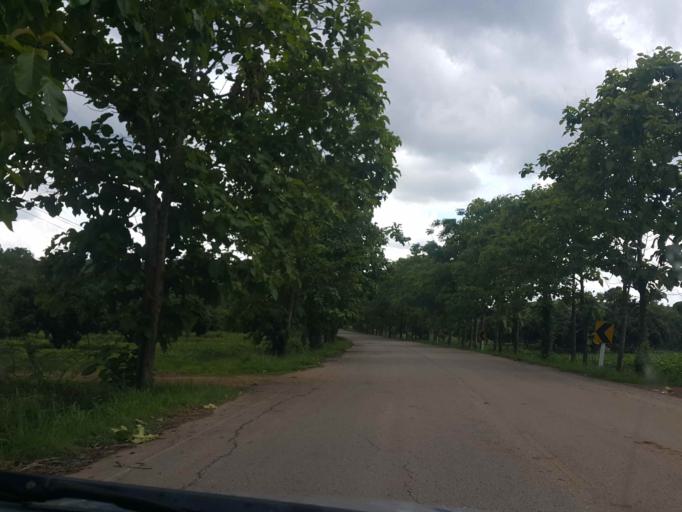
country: TH
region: Phayao
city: Dok Kham Tai
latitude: 18.9826
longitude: 100.0687
